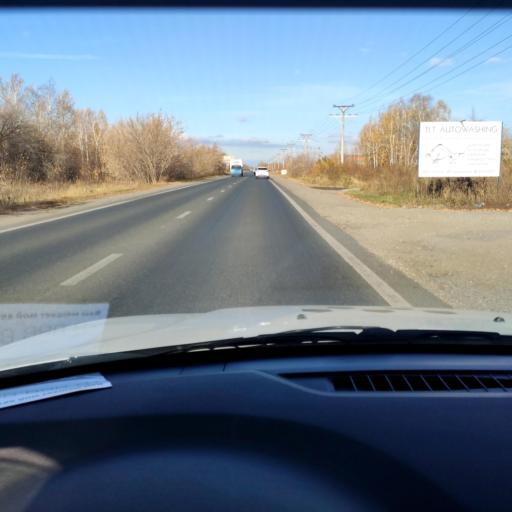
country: RU
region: Samara
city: Tol'yatti
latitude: 53.5545
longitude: 49.3669
